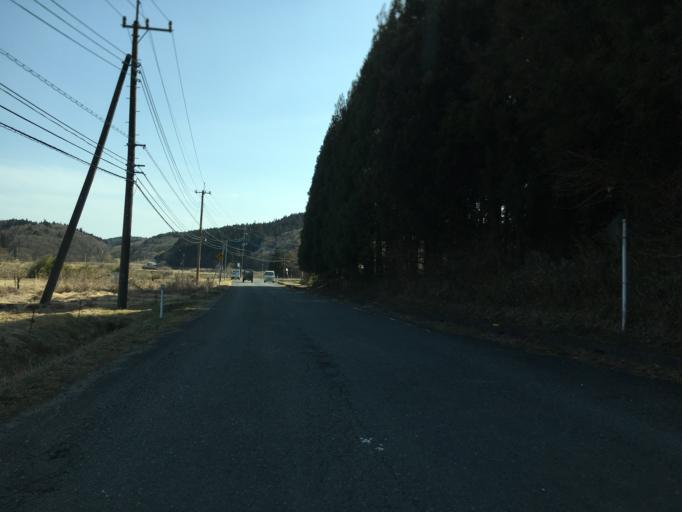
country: JP
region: Ibaraki
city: Takahagi
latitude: 36.7992
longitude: 140.5780
